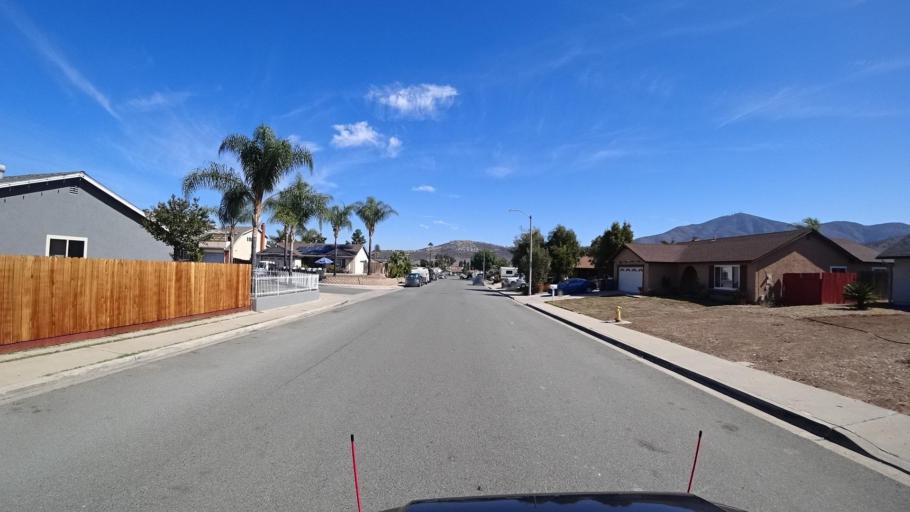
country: US
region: California
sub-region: San Diego County
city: La Presa
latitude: 32.7061
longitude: -116.9893
